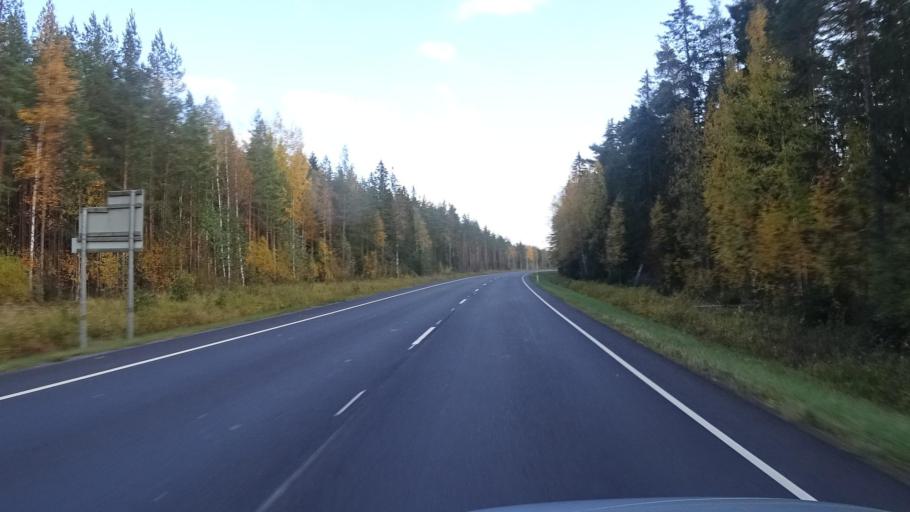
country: FI
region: Satakunta
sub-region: Rauma
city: Koeylioe
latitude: 61.1041
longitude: 22.2291
